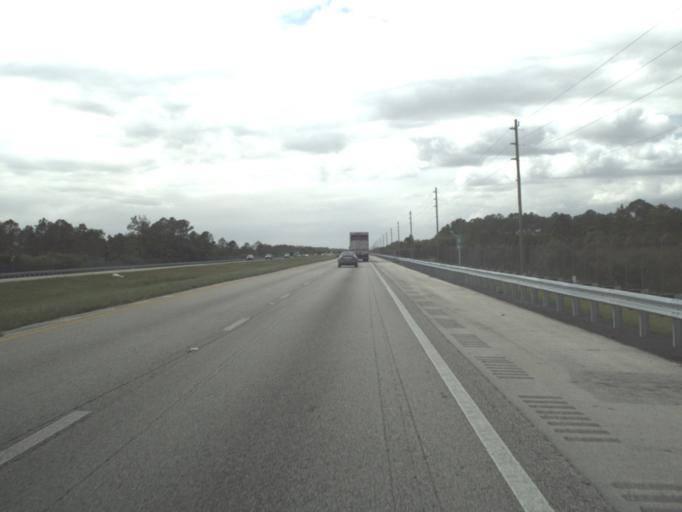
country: US
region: Florida
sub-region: Collier County
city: Immokalee
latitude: 26.1711
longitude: -80.9619
